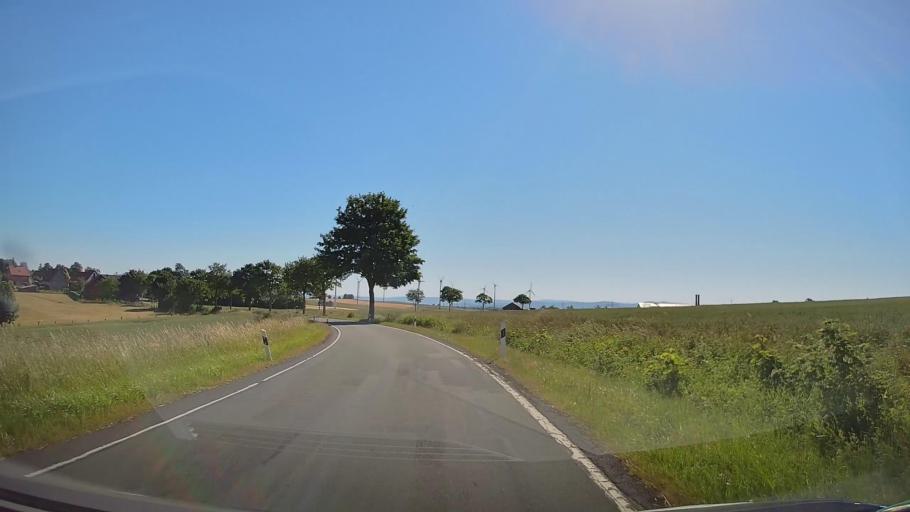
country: DE
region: Lower Saxony
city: Vahlbruch
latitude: 51.9589
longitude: 9.3291
